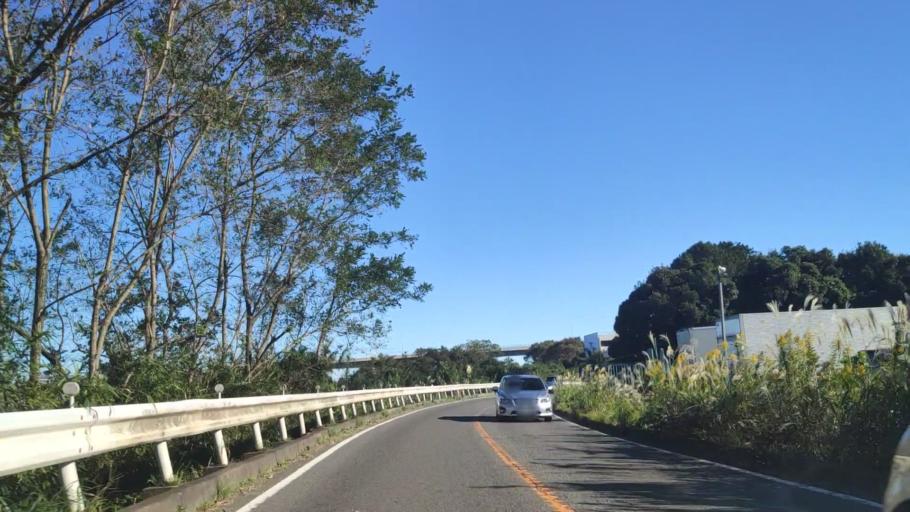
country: JP
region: Kanagawa
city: Zama
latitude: 35.5272
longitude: 139.3522
